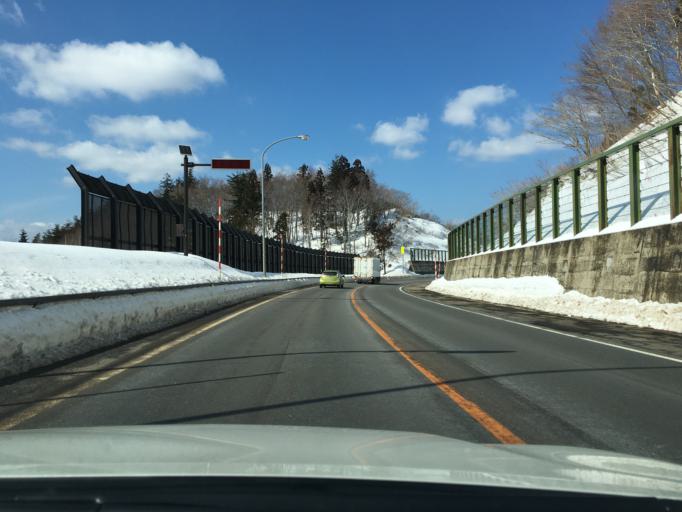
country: JP
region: Yamagata
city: Tsuruoka
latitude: 38.5569
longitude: 139.9294
